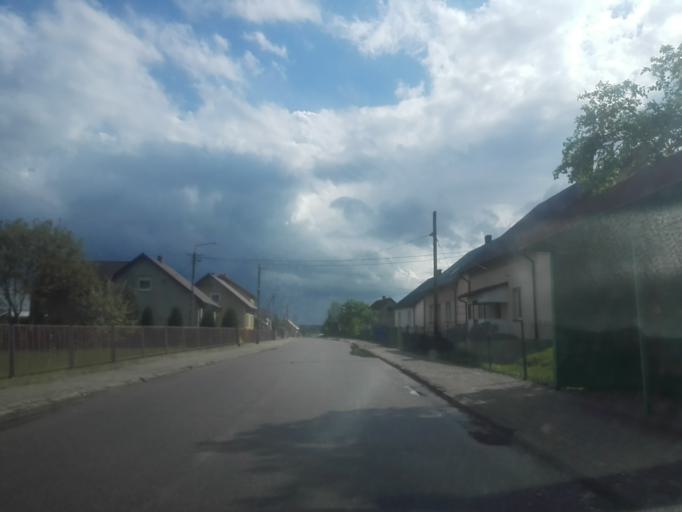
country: PL
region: Podlasie
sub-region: Powiat lomzynski
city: Wizna
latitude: 53.2258
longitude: 22.4200
